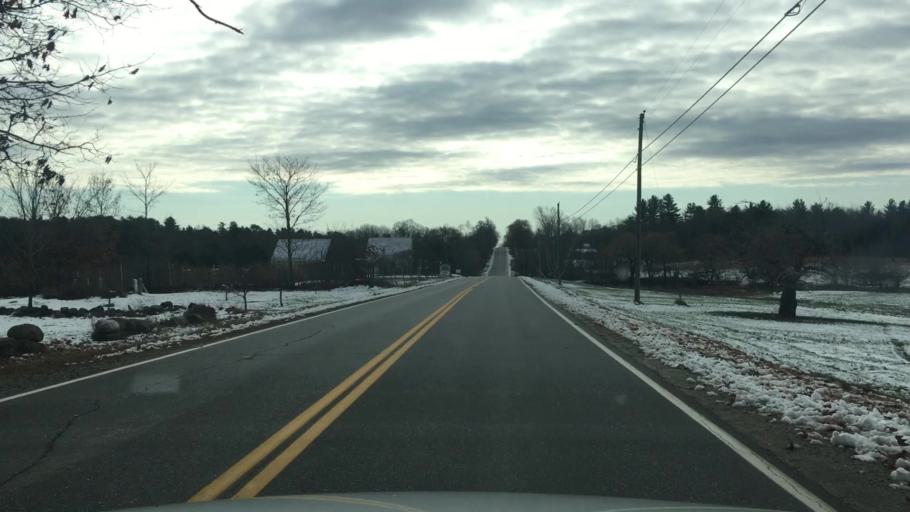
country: US
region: Maine
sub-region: Androscoggin County
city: Livermore
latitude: 44.3768
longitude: -70.2061
